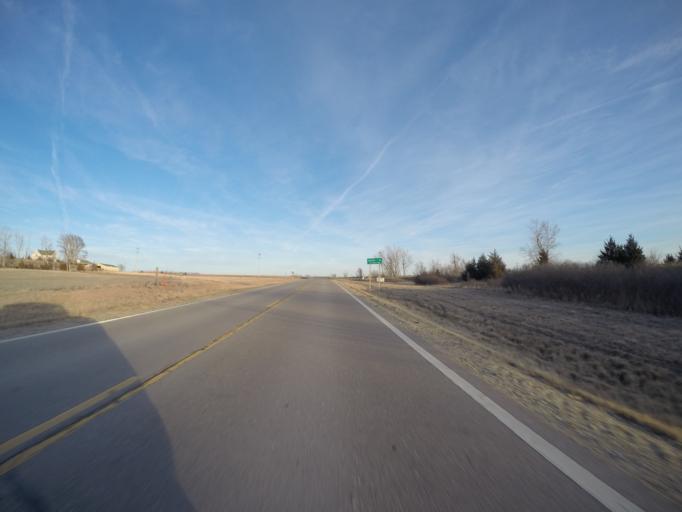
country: US
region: Kansas
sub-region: Dickinson County
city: Herington
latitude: 38.6611
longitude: -96.8578
